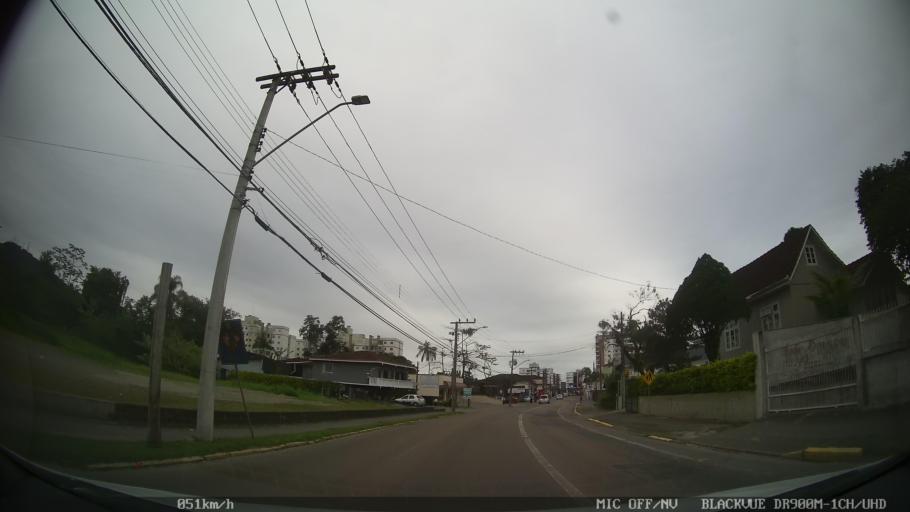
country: BR
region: Santa Catarina
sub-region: Joinville
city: Joinville
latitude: -26.2805
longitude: -48.8372
